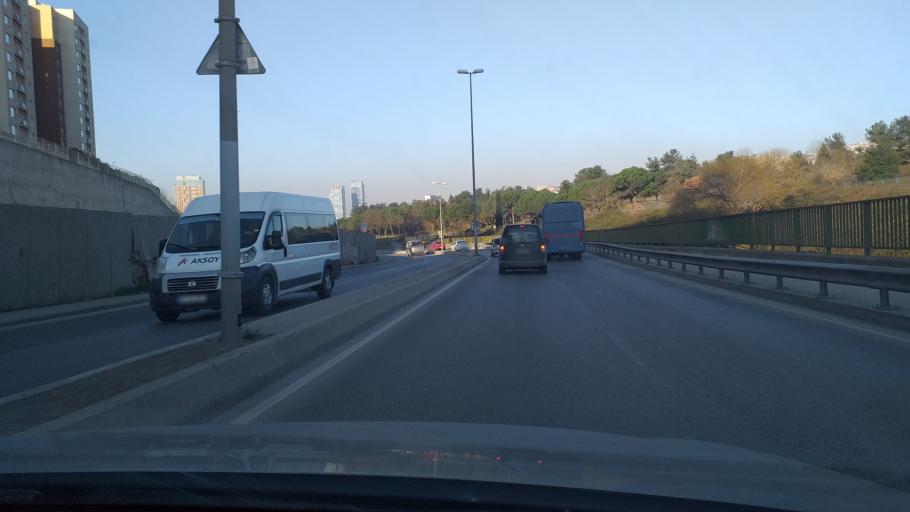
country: TR
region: Istanbul
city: Maltepe
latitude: 40.9213
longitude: 29.1844
